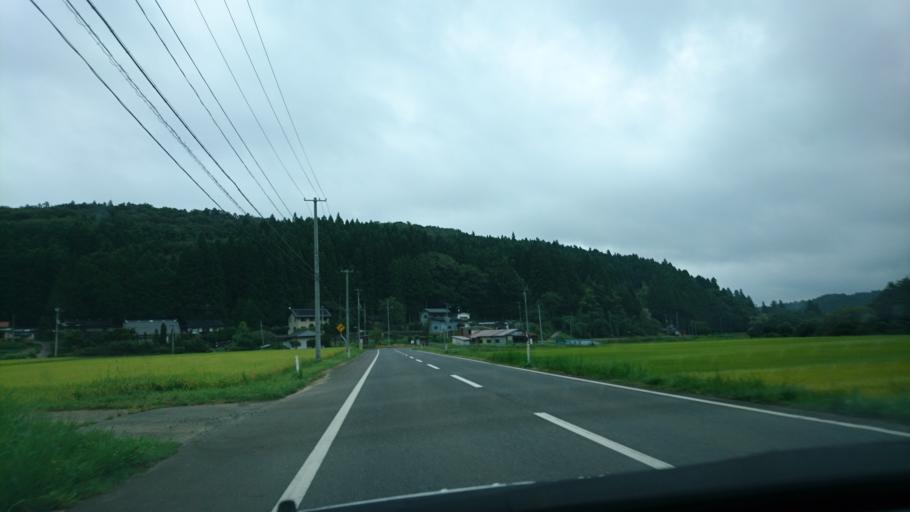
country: JP
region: Iwate
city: Ichinoseki
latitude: 38.9101
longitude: 141.0536
